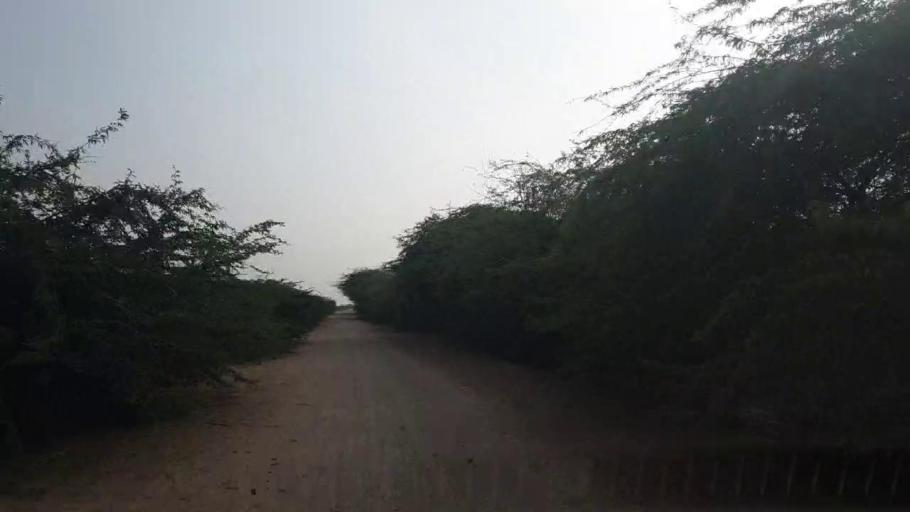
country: PK
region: Sindh
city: Badin
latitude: 24.6347
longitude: 68.6925
